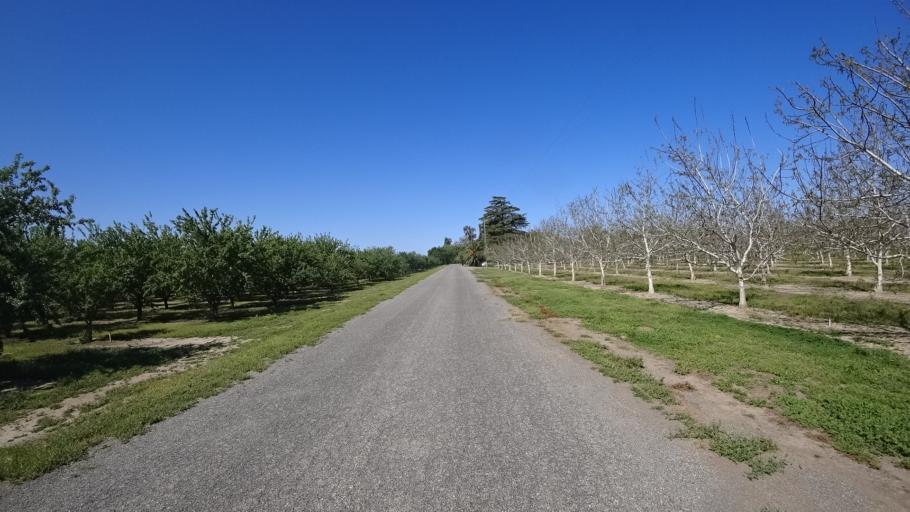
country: US
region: California
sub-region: Glenn County
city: Hamilton City
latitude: 39.7286
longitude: -122.0262
